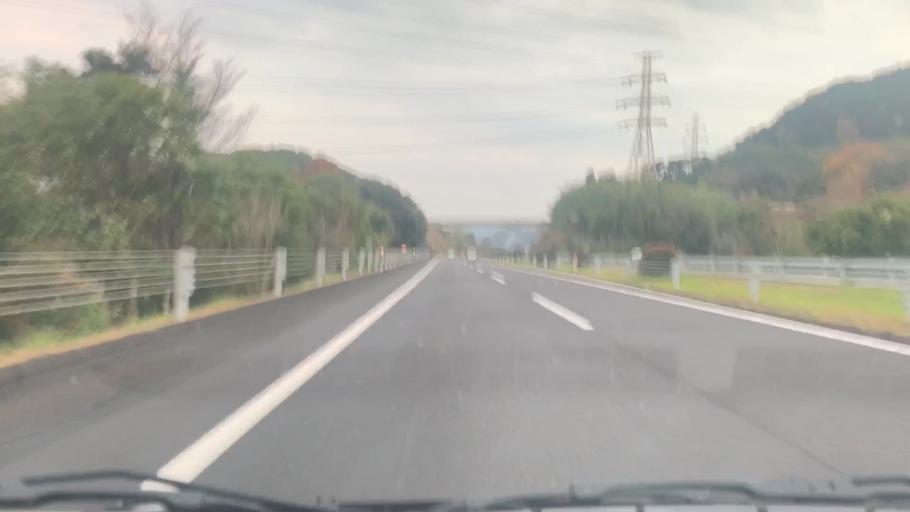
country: JP
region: Nagasaki
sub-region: Isahaya-shi
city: Isahaya
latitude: 32.8590
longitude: 130.0044
